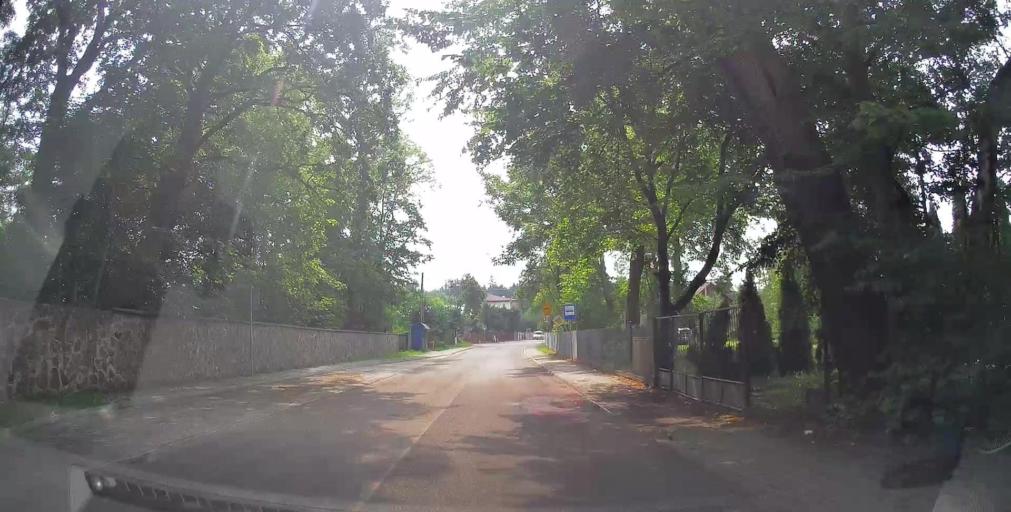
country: PL
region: Masovian Voivodeship
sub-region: Powiat bialobrzeski
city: Sucha
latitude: 51.6206
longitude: 20.9505
